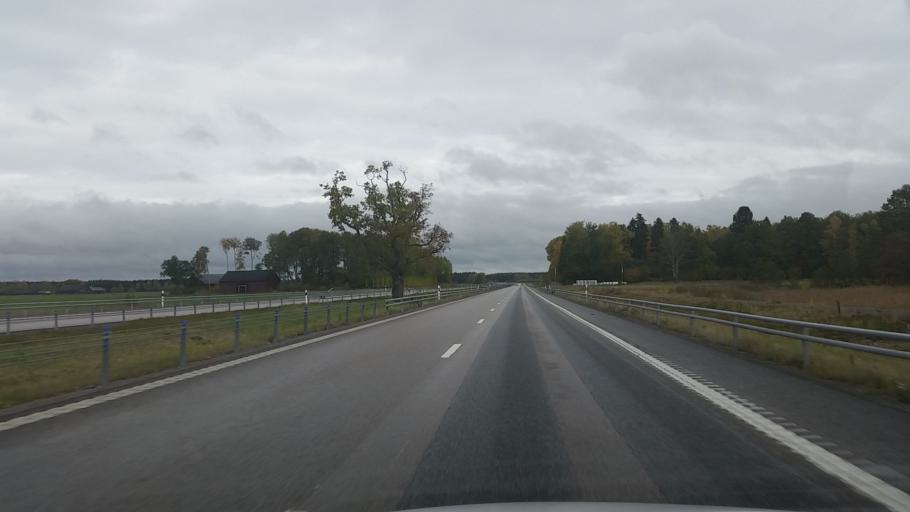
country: SE
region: Uppsala
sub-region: Osthammars Kommun
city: Bjorklinge
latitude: 60.0592
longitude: 17.6136
